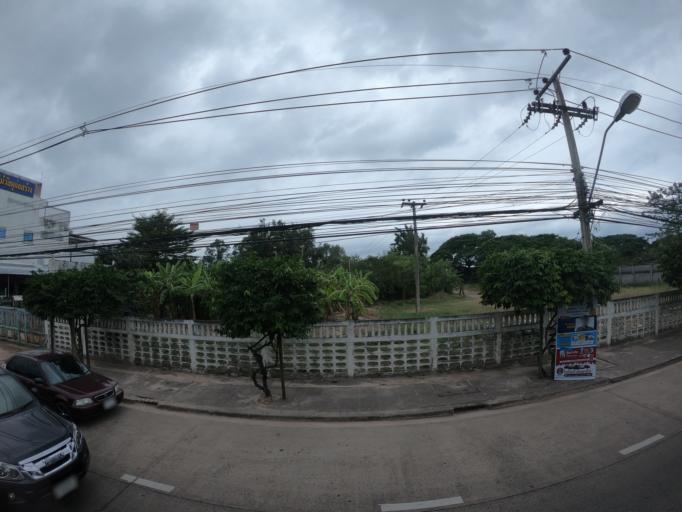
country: TH
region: Roi Et
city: Roi Et
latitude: 16.0524
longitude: 103.6416
